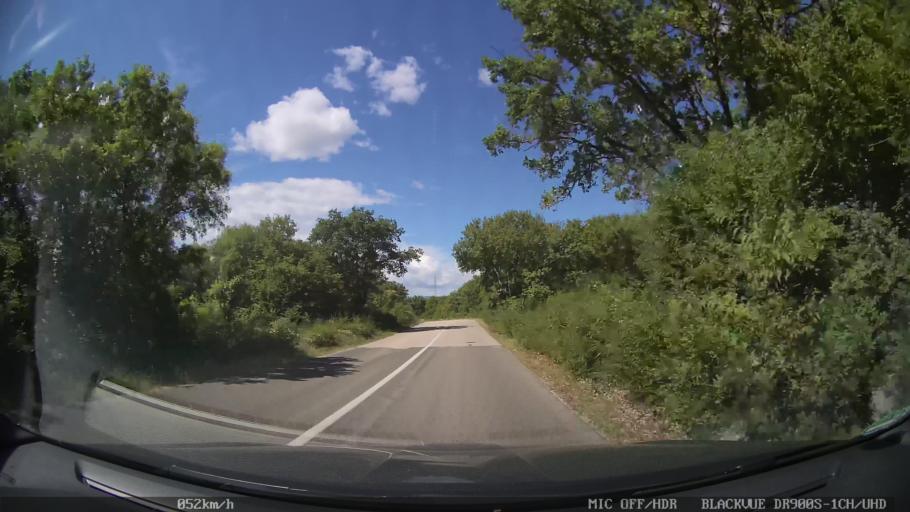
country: HR
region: Primorsko-Goranska
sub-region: Grad Krk
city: Krk
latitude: 45.0503
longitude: 14.5055
